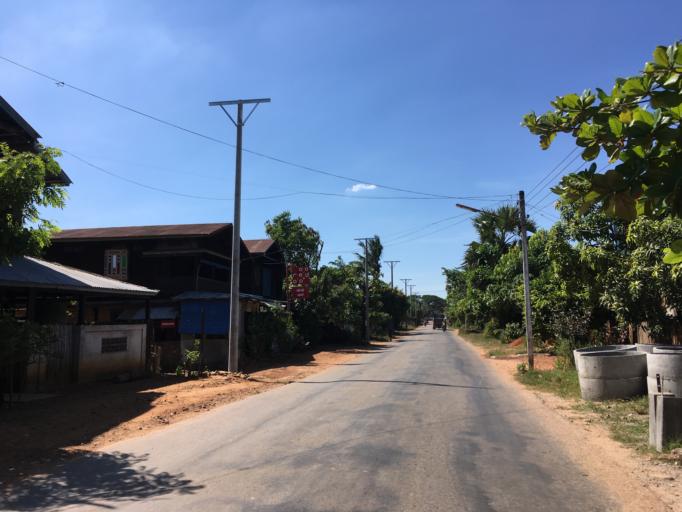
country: MM
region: Mon
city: Kyaikkami
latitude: 15.5082
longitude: 97.8440
